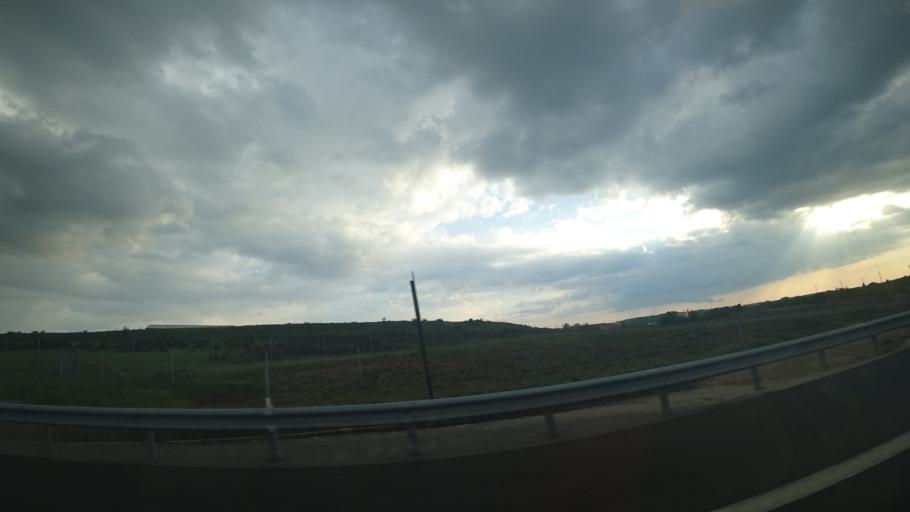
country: FR
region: Midi-Pyrenees
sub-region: Departement de l'Aveyron
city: La Cavalerie
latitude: 44.0154
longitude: 3.1360
